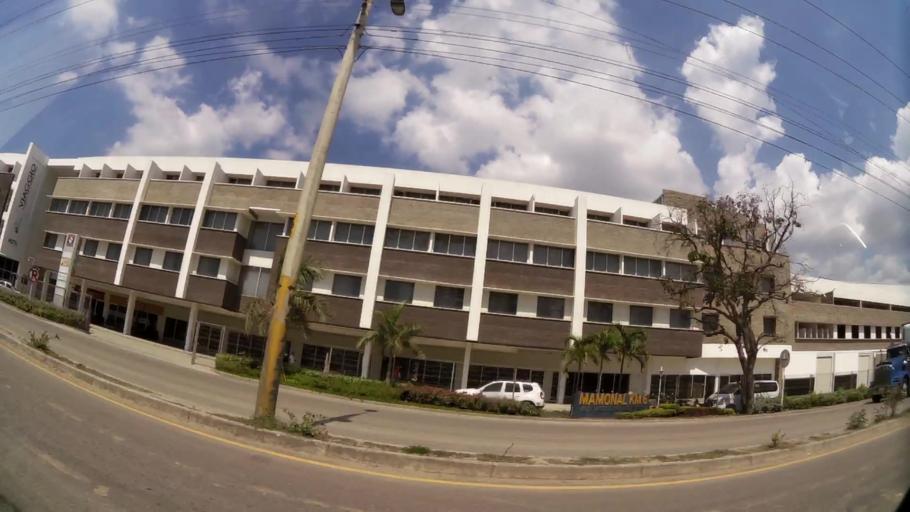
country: CO
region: Bolivar
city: Cartagena
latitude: 10.3424
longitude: -75.4935
